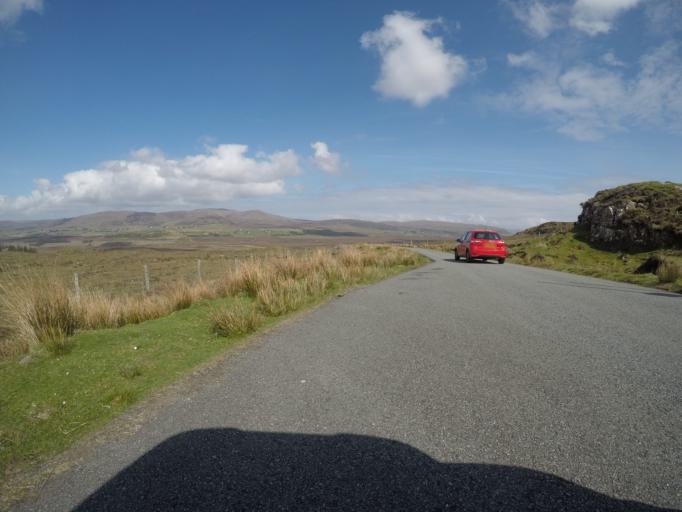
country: GB
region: Scotland
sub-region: Highland
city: Isle of Skye
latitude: 57.4227
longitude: -6.2694
